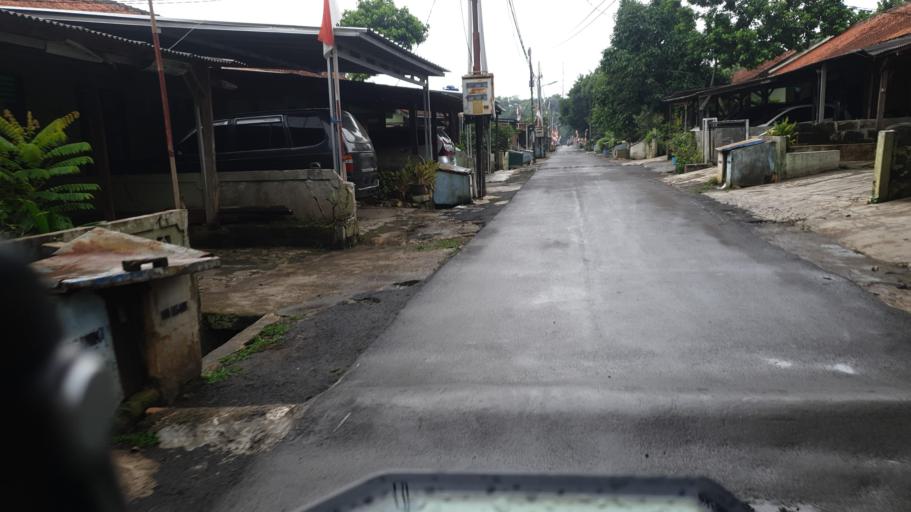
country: ID
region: West Java
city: Depok
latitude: -6.3439
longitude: 106.8312
